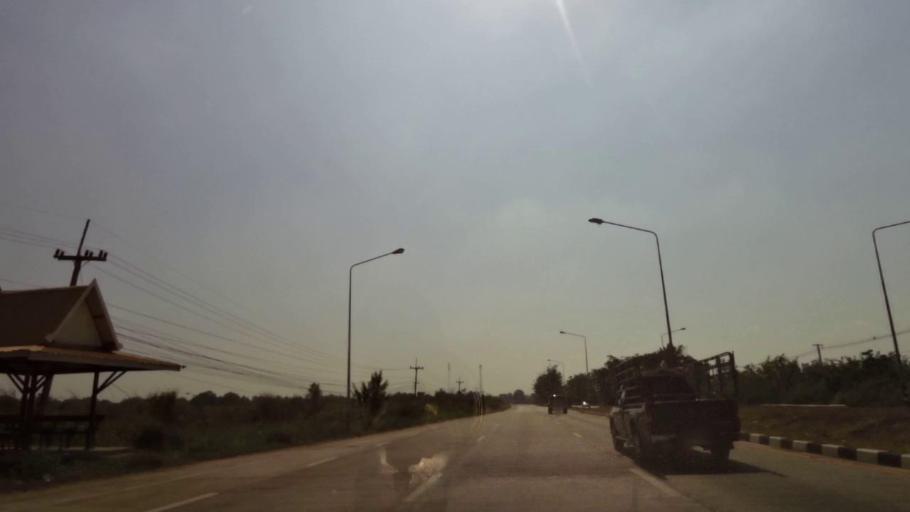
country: TH
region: Phichit
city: Wachira Barami
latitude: 16.3528
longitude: 100.1290
